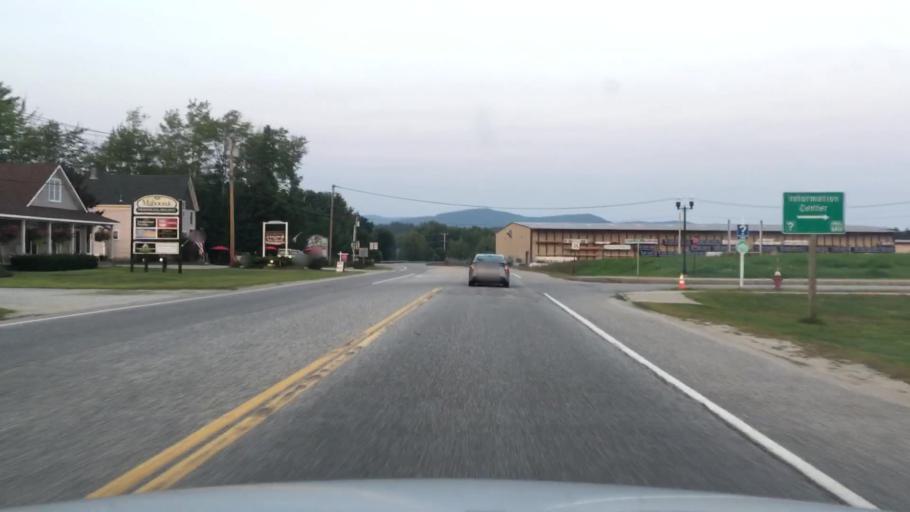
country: US
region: Maine
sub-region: Oxford County
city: Bethel
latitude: 44.4125
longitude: -70.7943
